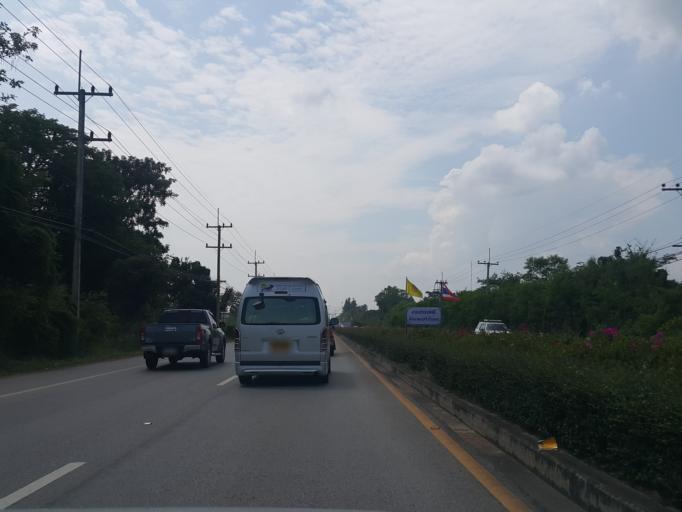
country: TH
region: Chiang Mai
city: Doi Lo
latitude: 18.4775
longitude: 98.7962
